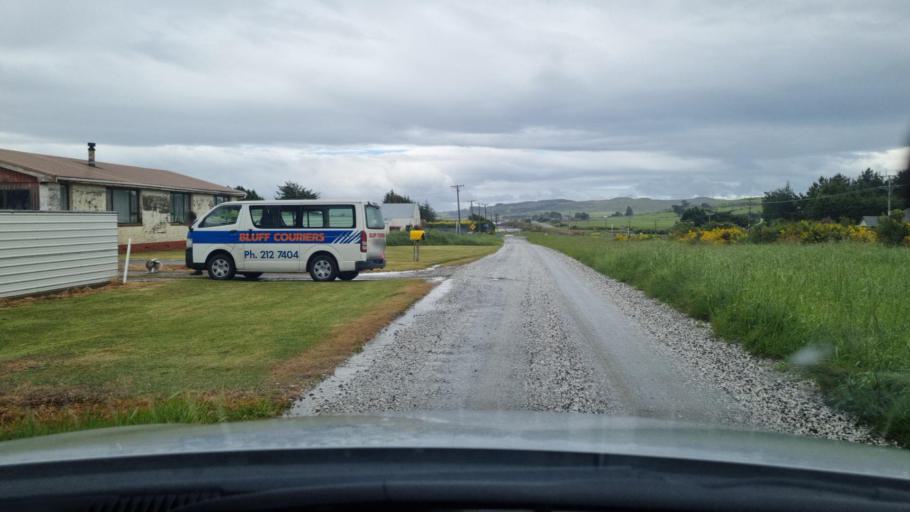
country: NZ
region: Southland
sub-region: Invercargill City
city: Bluff
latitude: -46.5453
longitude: 168.3014
